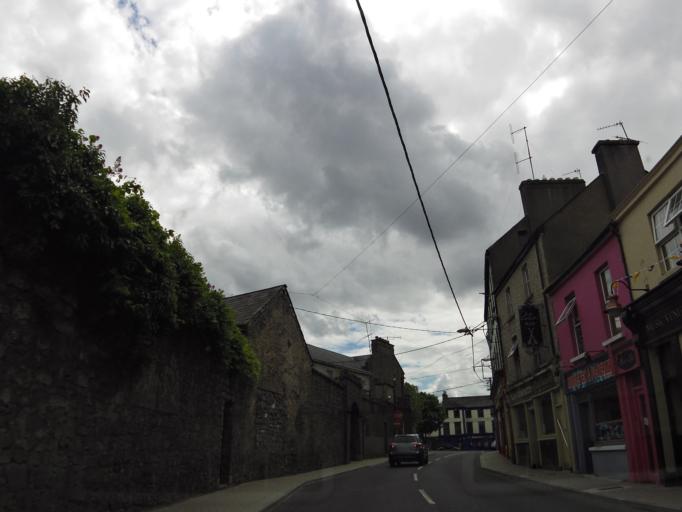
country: IE
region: Munster
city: Thurles
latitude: 52.6796
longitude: -7.8149
